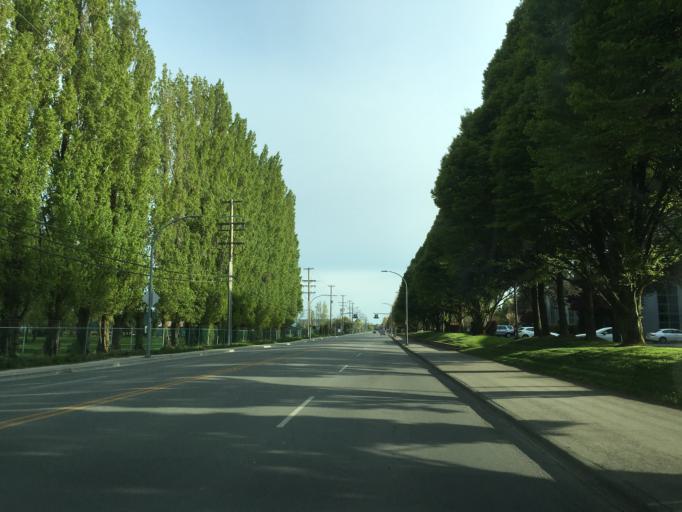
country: CA
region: British Columbia
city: Richmond
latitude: 49.1760
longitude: -123.0693
